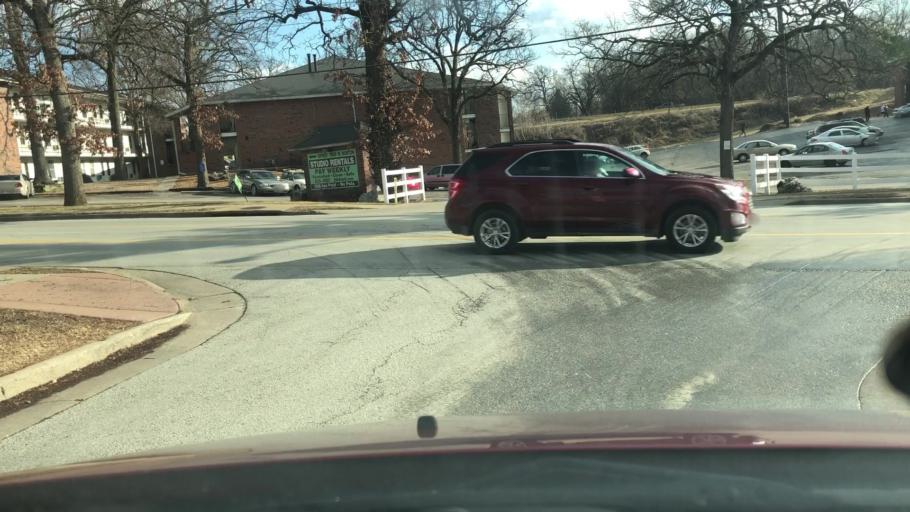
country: US
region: Missouri
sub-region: Greene County
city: Springfield
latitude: 37.2519
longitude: -93.3027
